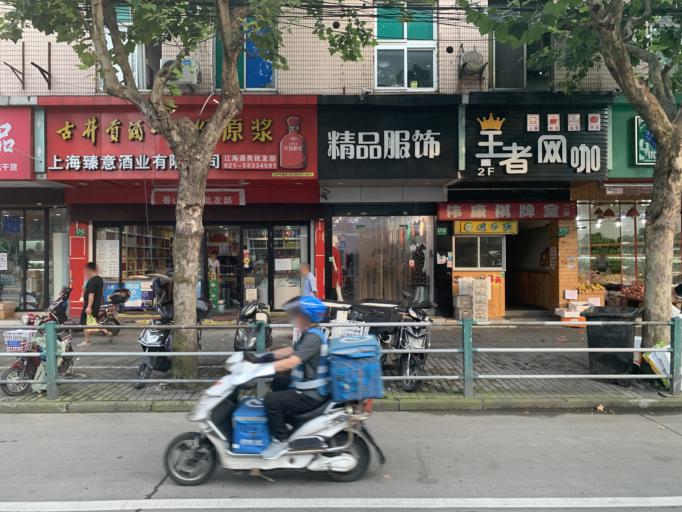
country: CN
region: Shanghai Shi
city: Pudong
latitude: 31.2431
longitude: 121.5653
